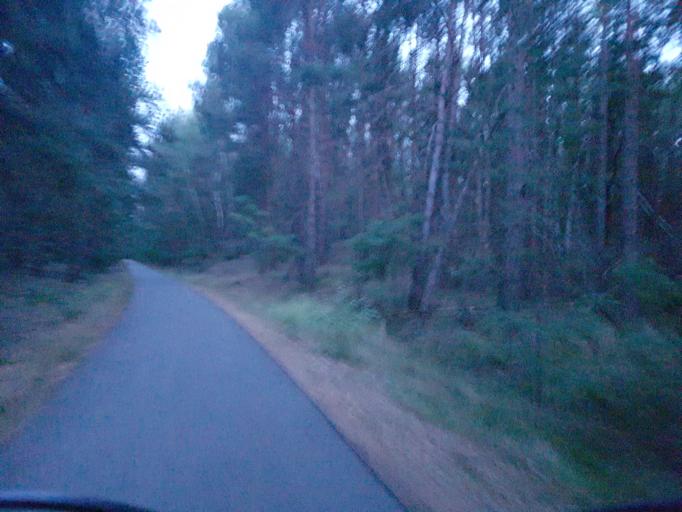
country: DE
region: Brandenburg
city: Trobitz
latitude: 51.5692
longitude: 13.4391
